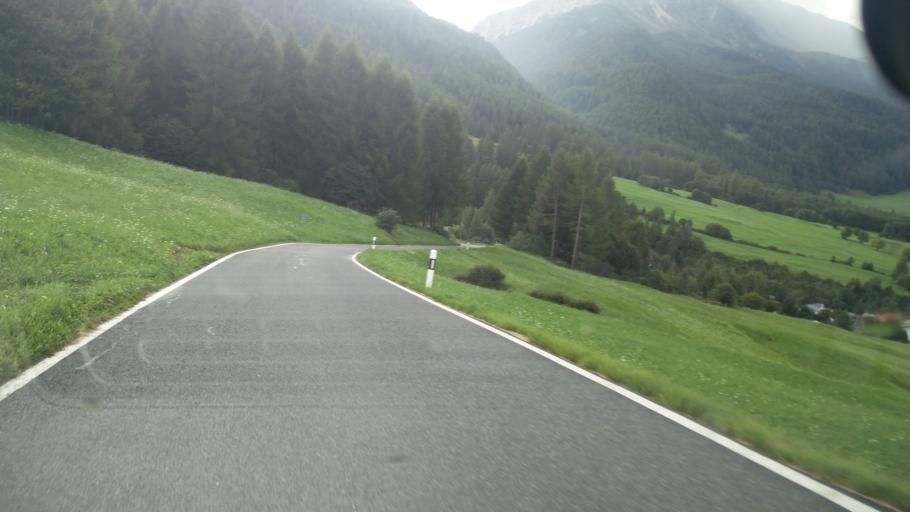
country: IT
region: Trentino-Alto Adige
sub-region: Bolzano
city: Tubre
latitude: 46.5998
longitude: 10.4305
